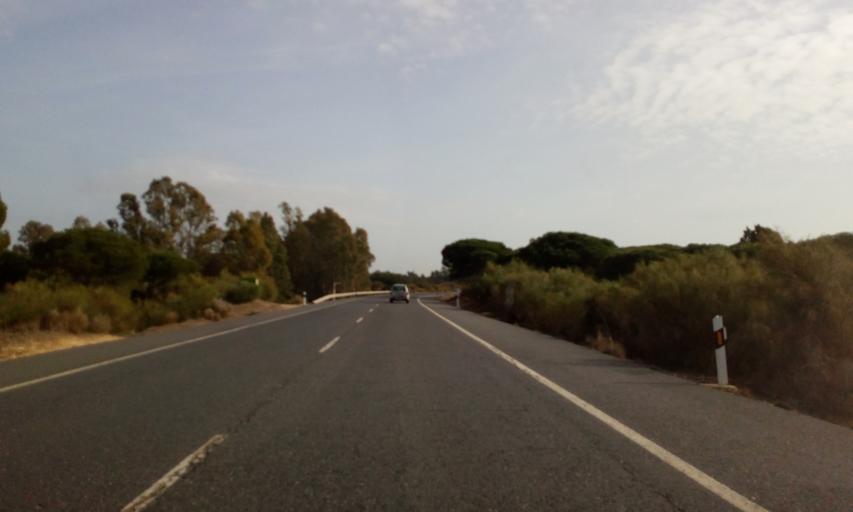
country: ES
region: Andalusia
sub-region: Provincia de Huelva
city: Palos de la Frontera
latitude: 37.1578
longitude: -6.8769
